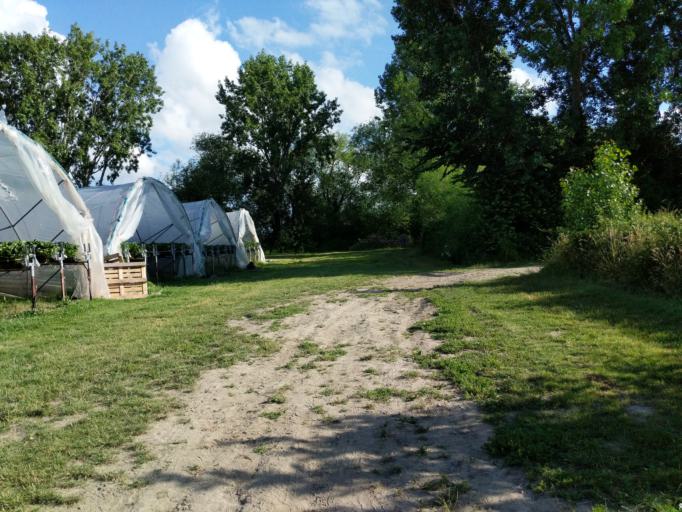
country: GB
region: England
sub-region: Kent
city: Faversham
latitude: 51.3308
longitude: 0.9198
